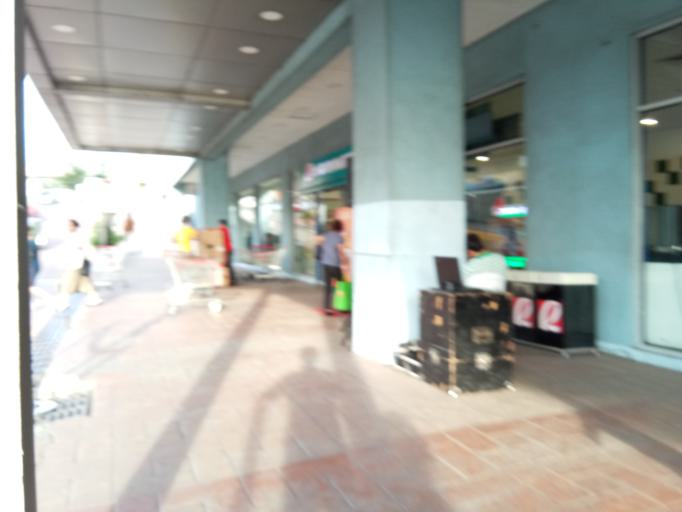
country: PH
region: Calabarzon
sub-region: Province of Cavite
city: Dasmarinas
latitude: 14.3008
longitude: 120.9535
